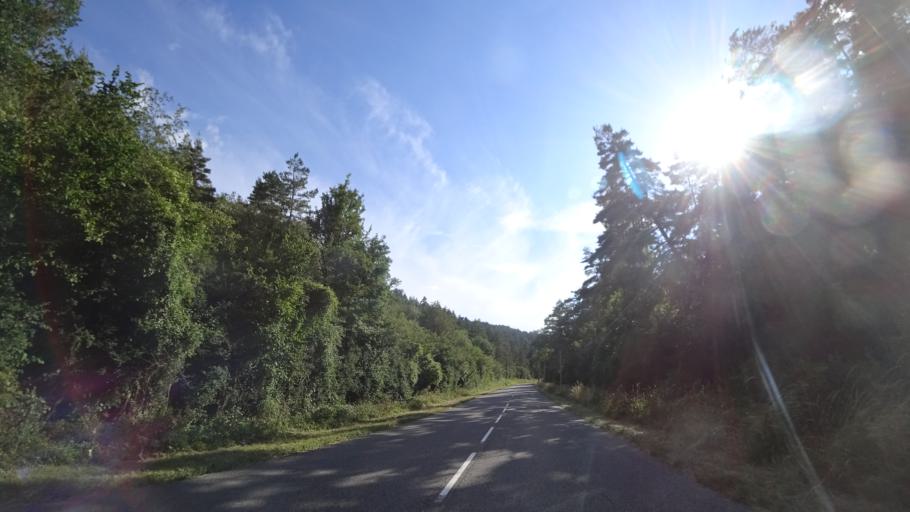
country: FR
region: Languedoc-Roussillon
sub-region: Departement de la Lozere
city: La Canourgue
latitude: 44.4108
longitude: 3.2641
